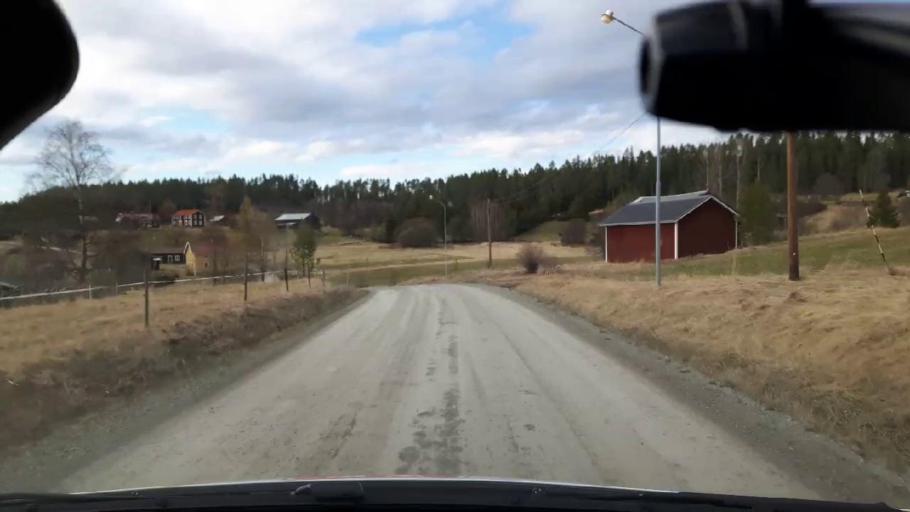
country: SE
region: Jaemtland
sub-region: OEstersunds Kommun
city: Brunflo
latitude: 62.9515
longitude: 14.6580
